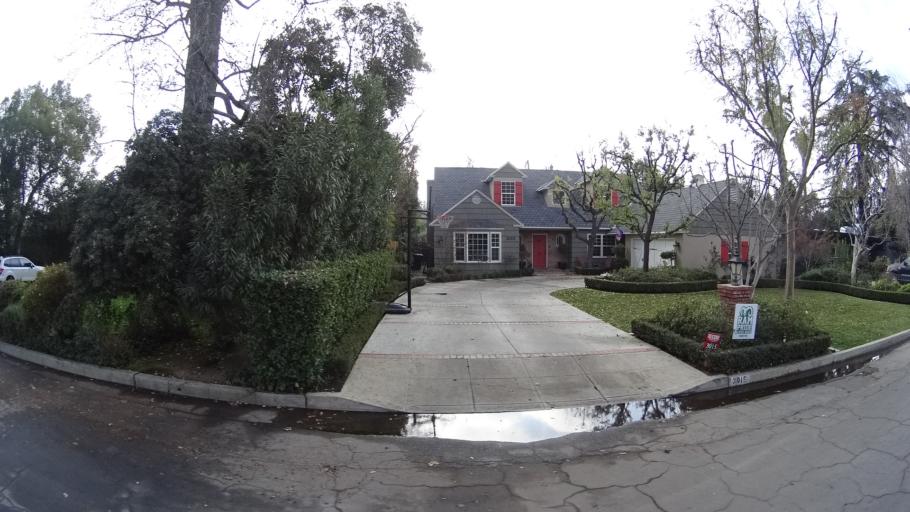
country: US
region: California
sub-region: Kern County
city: Bakersfield
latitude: 35.3772
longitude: -119.0369
